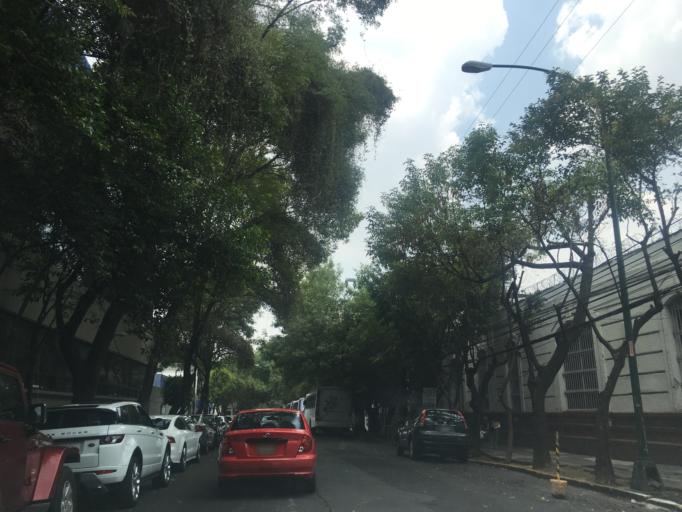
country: MX
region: Mexico City
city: Polanco
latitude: 19.4088
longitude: -99.1814
